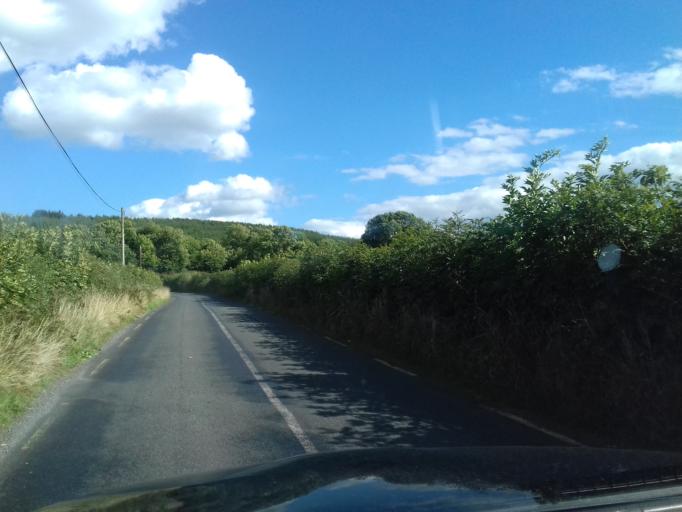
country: IE
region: Leinster
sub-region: Kilkenny
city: Thomastown
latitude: 52.5491
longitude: -7.0767
